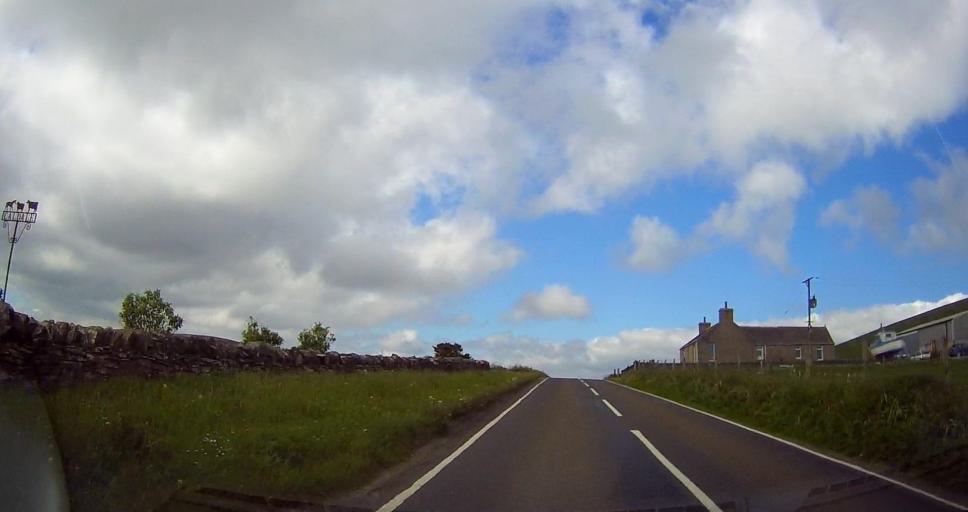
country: GB
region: Scotland
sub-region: Orkney Islands
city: Orkney
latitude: 58.9790
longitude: -3.0217
